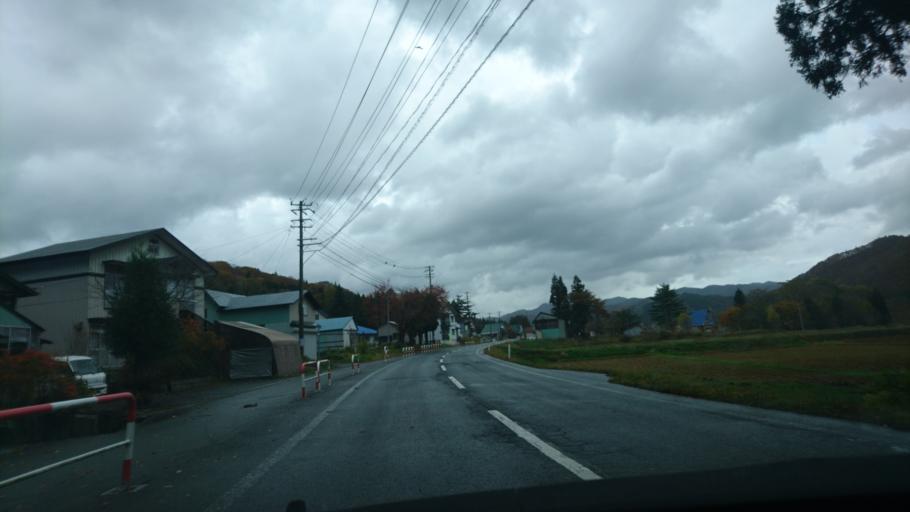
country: JP
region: Akita
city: Kakunodatemachi
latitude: 39.4773
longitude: 140.7911
